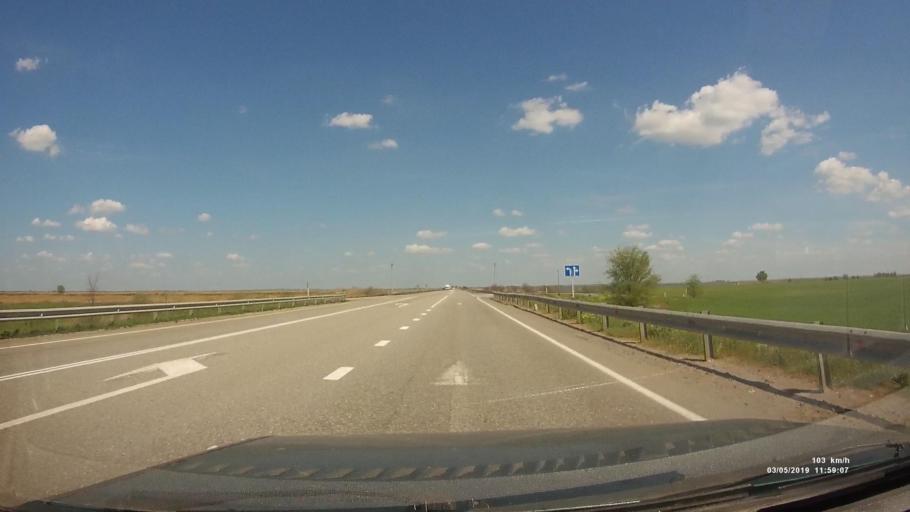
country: RU
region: Rostov
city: Bagayevskaya
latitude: 47.2305
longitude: 40.3272
